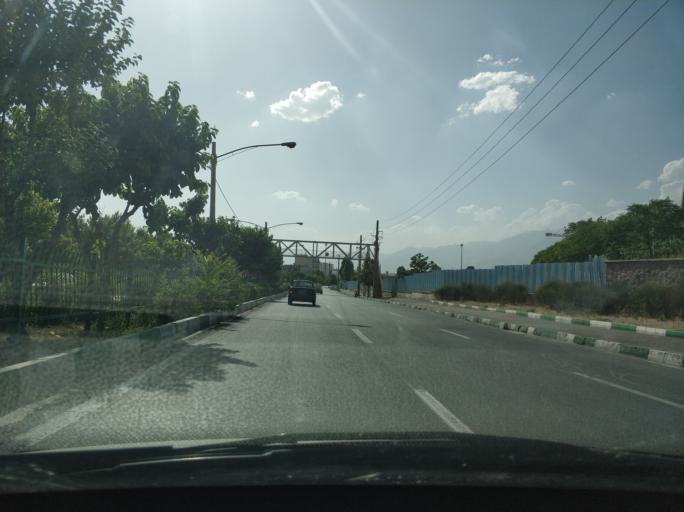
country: IR
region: Tehran
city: Tajrish
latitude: 35.7456
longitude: 51.5742
